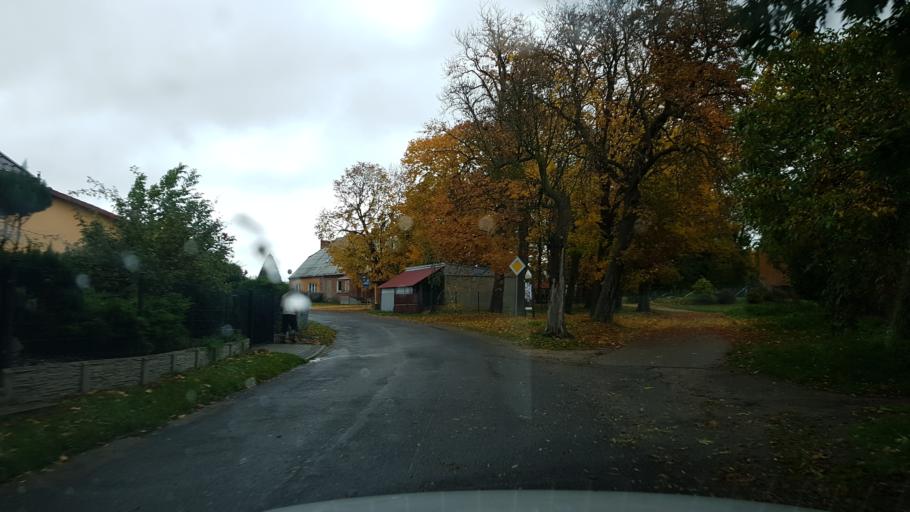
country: PL
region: West Pomeranian Voivodeship
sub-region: Powiat mysliborski
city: Mysliborz
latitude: 52.9737
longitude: 14.8844
